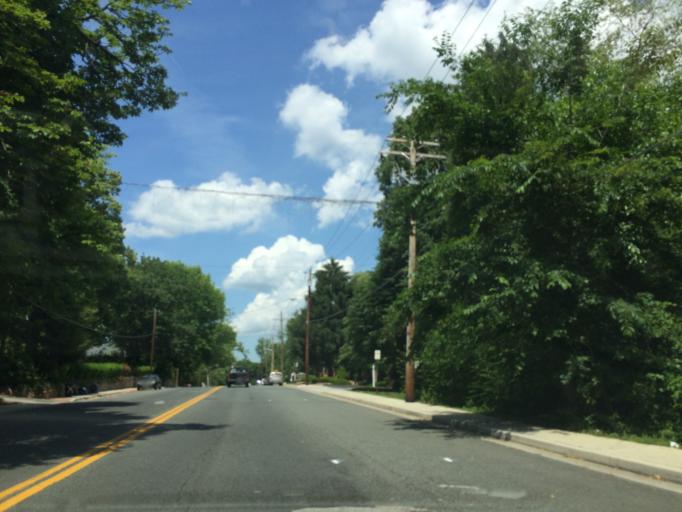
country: US
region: Maryland
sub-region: Baltimore County
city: Charlestown
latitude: 39.2834
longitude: -76.7147
